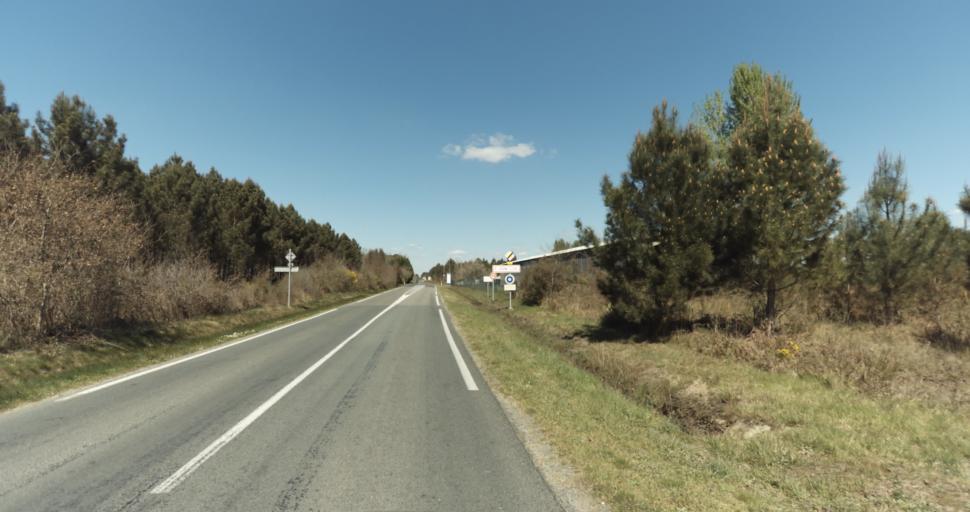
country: FR
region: Aquitaine
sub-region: Departement de la Gironde
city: Martignas-sur-Jalle
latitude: 44.7932
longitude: -0.7764
